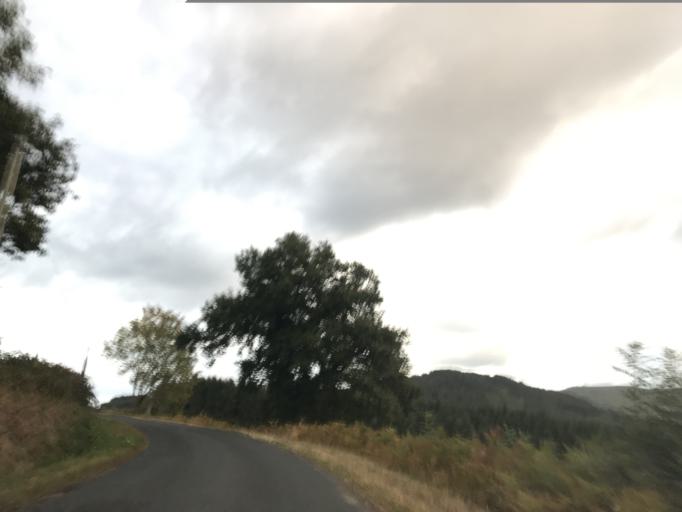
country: FR
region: Auvergne
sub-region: Departement du Puy-de-Dome
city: Celles-sur-Durolle
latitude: 45.8404
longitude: 3.6278
